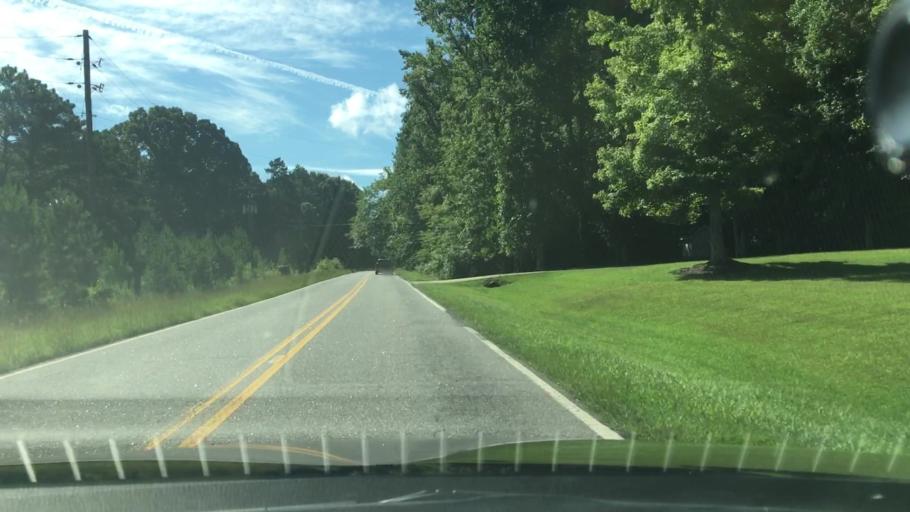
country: US
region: Georgia
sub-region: Putnam County
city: Jefferson
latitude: 33.3849
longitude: -83.2581
